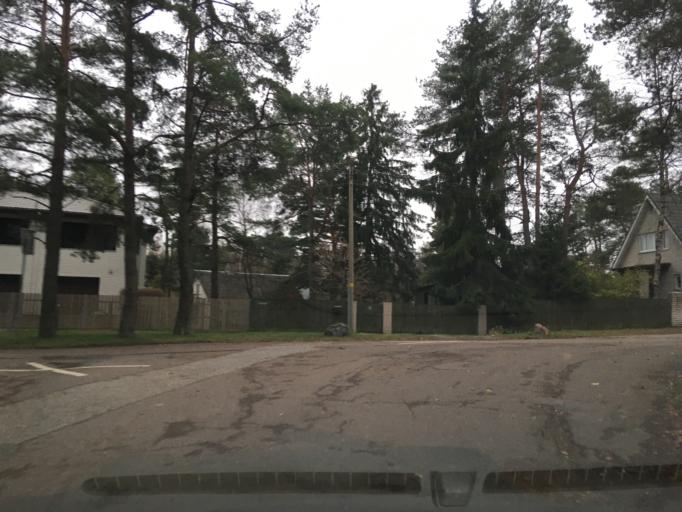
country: EE
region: Harju
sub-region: Saku vald
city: Saku
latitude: 59.3724
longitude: 24.6993
